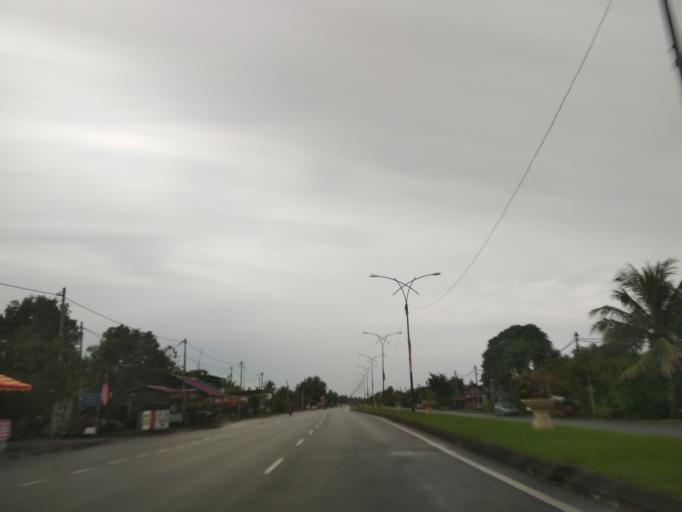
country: MY
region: Perlis
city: Kangar
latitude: 6.4563
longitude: 100.2073
